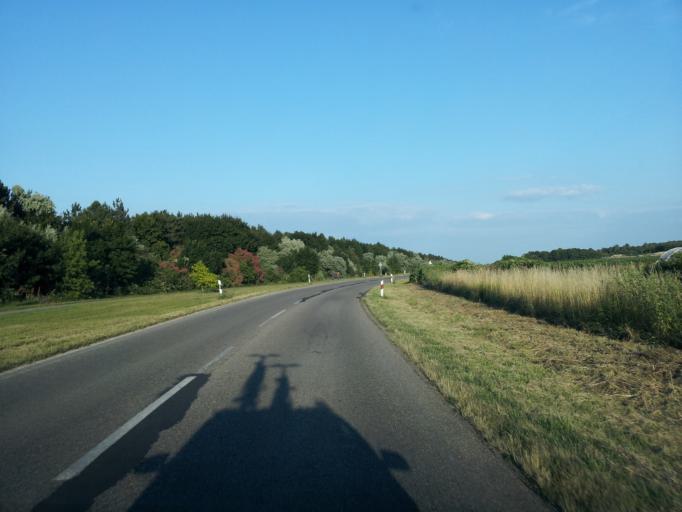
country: HU
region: Veszprem
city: Szentkiralyszabadja
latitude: 47.0722
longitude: 17.9418
